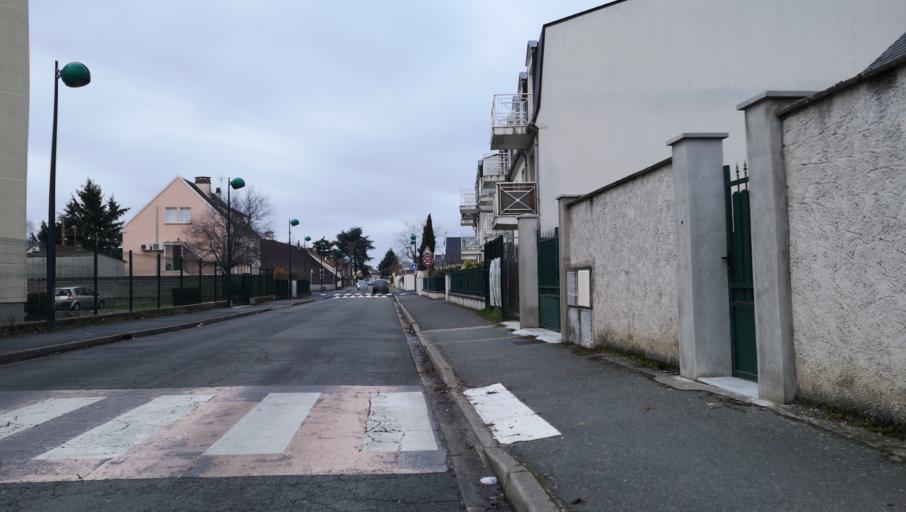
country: FR
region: Centre
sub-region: Departement du Loiret
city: Saint-Jean-de-Braye
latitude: 47.9114
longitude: 1.9628
